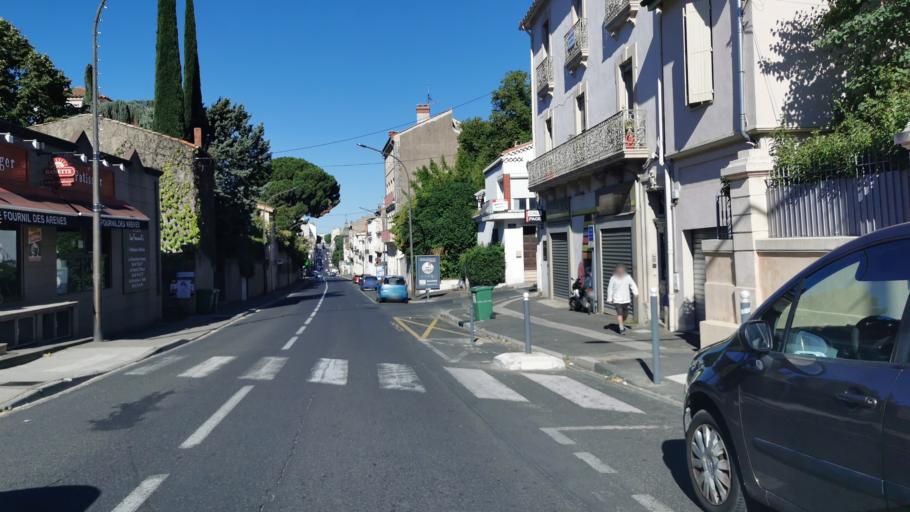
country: FR
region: Languedoc-Roussillon
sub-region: Departement de l'Herault
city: Beziers
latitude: 43.3440
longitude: 3.2273
